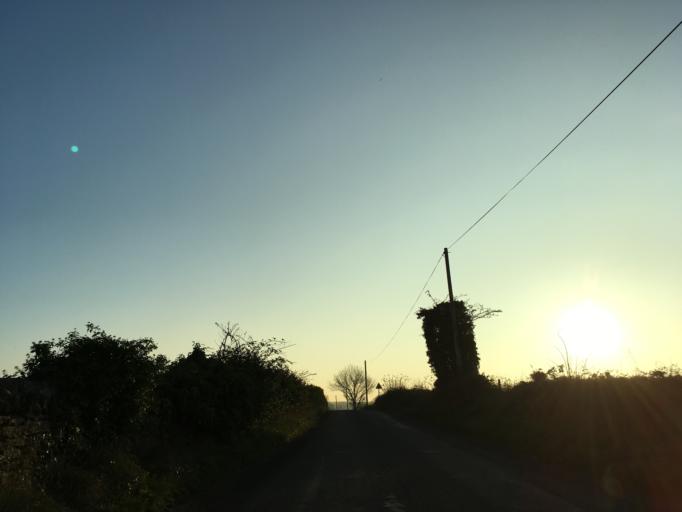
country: GB
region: England
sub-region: Wiltshire
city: Nettleton
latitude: 51.4709
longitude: -2.2749
